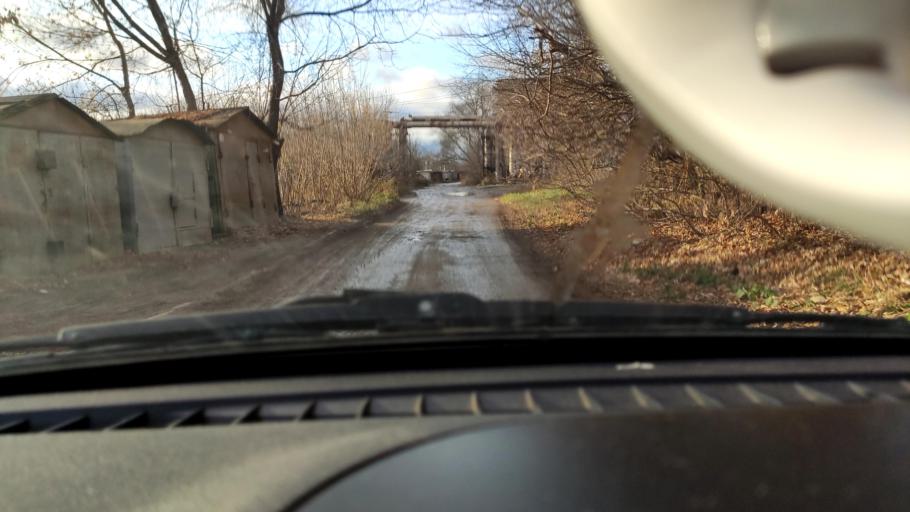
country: RU
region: Perm
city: Kondratovo
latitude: 57.9590
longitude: 56.1482
